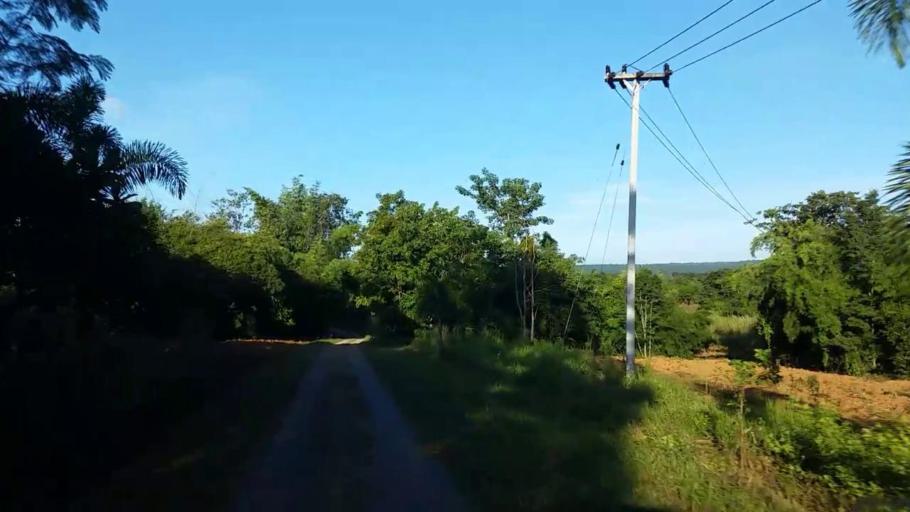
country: TH
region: Chaiyaphum
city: Thep Sathit
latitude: 15.5490
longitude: 101.4786
